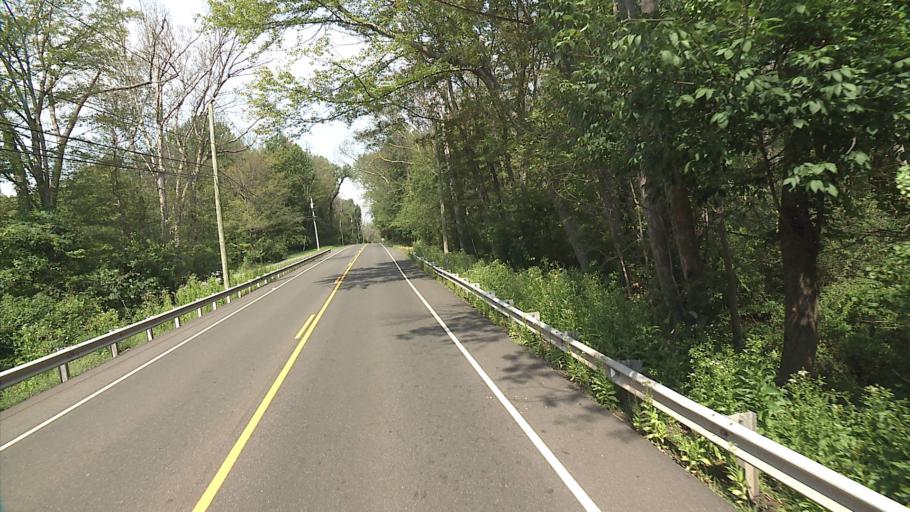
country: US
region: Connecticut
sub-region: Middlesex County
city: Durham
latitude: 41.4518
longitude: -72.6684
